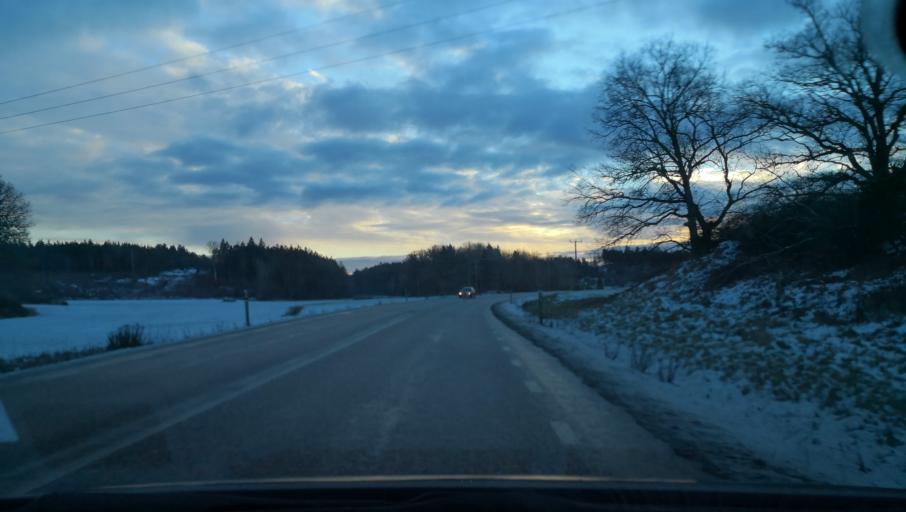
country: SE
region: Soedermanland
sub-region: Eskilstuna Kommun
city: Skogstorp
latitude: 59.3444
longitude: 16.4648
